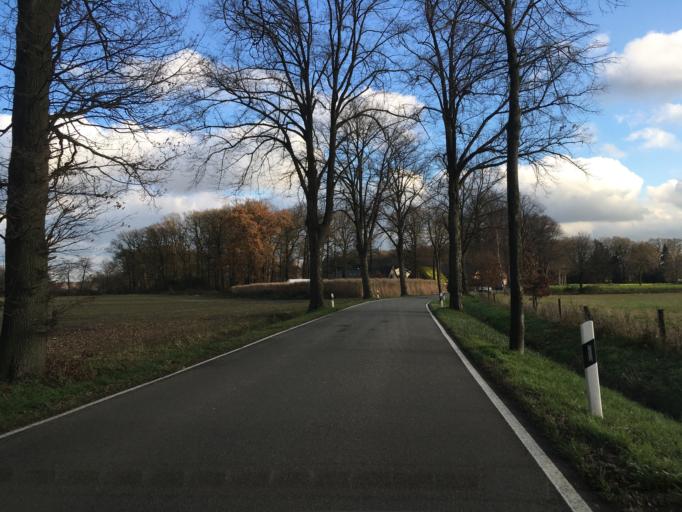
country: DE
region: North Rhine-Westphalia
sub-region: Regierungsbezirk Munster
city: Gescher
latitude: 51.9548
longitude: 7.0624
